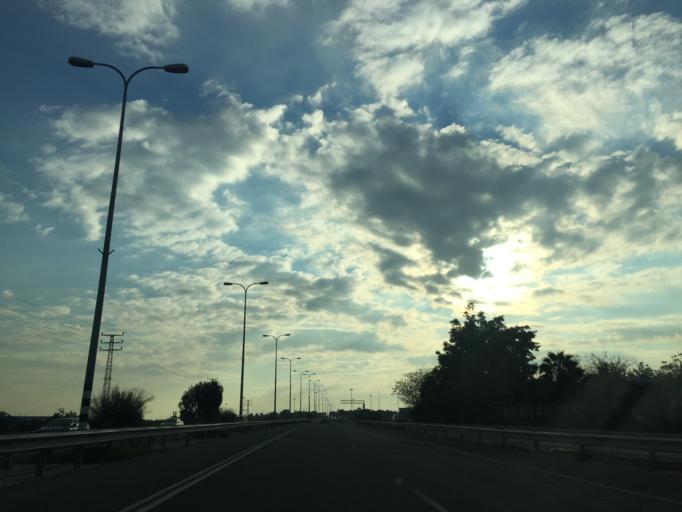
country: IL
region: Central District
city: Lod
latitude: 31.9296
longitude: 34.8892
